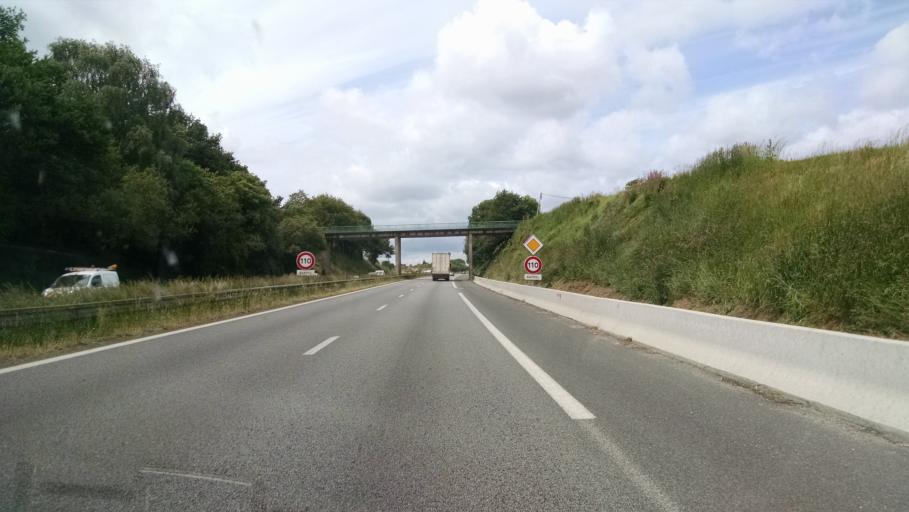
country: FR
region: Brittany
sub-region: Departement du Morbihan
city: Arradon
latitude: 47.6607
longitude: -2.8156
